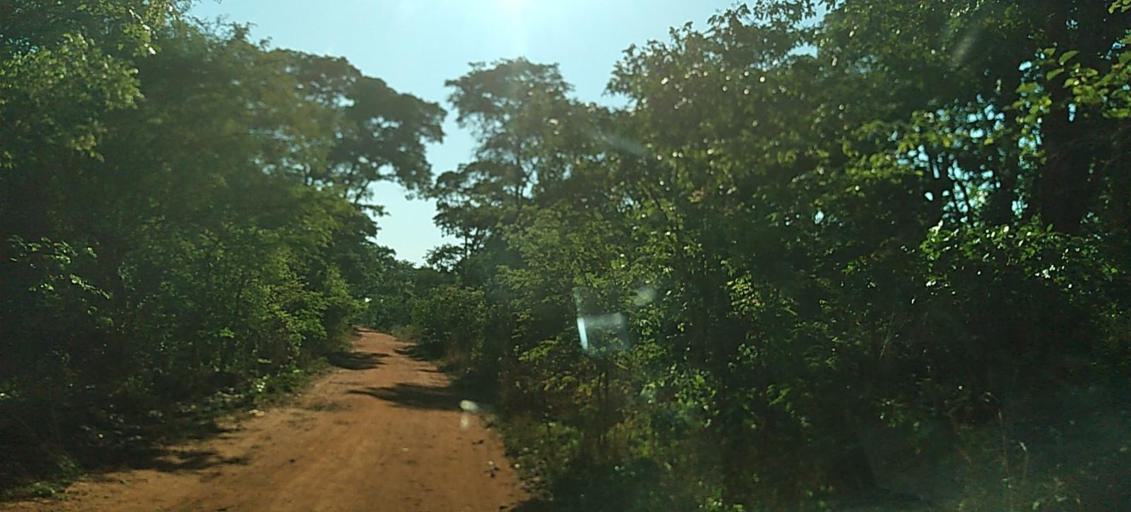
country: ZM
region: Copperbelt
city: Luanshya
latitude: -13.4589
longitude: 28.8288
